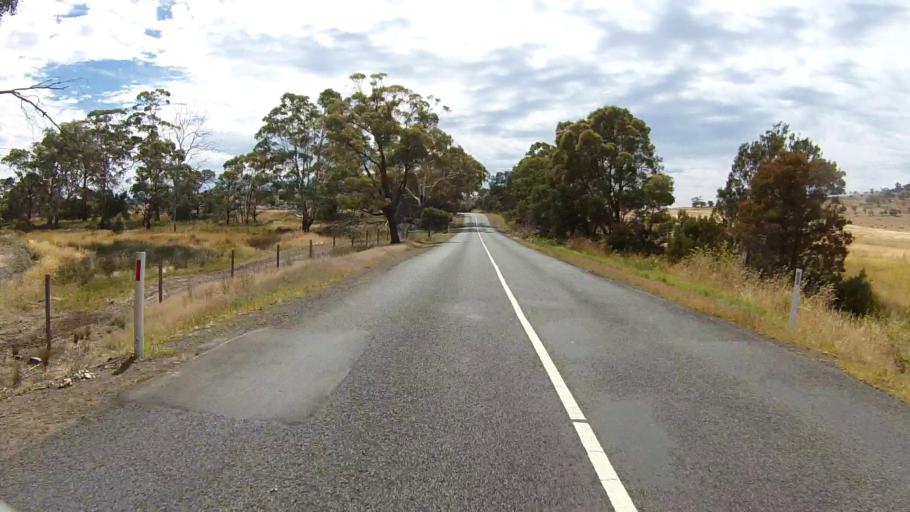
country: AU
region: Tasmania
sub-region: Sorell
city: Sorell
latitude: -42.8765
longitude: 147.6785
